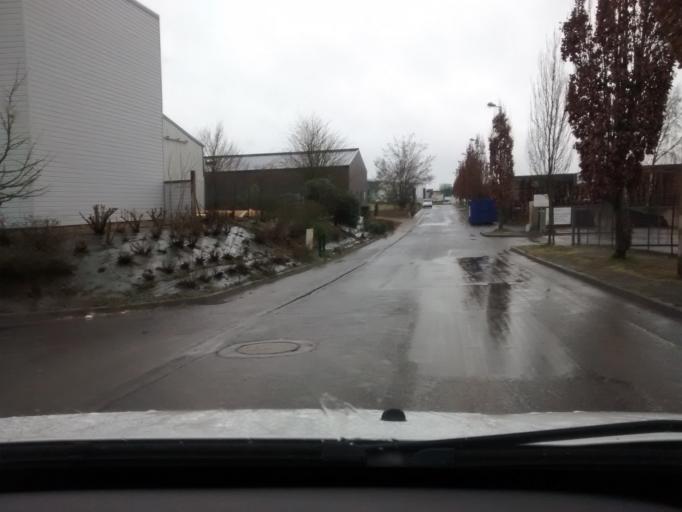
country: FR
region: Brittany
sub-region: Departement d'Ille-et-Vilaine
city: Acigne
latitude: 48.1380
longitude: -1.5176
